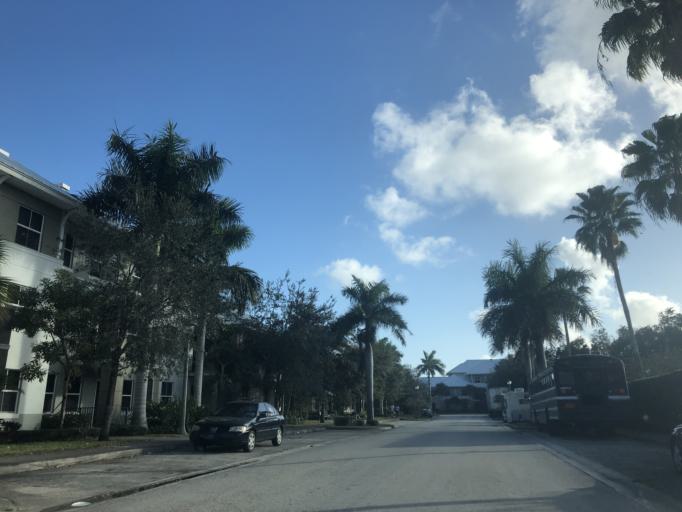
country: US
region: Florida
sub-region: Palm Beach County
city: West Palm Beach
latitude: 26.7207
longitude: -80.0800
